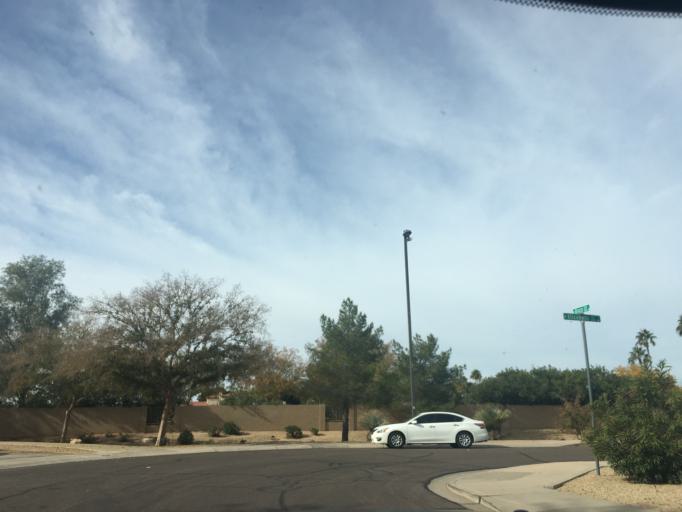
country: US
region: Arizona
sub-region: Maricopa County
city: Gilbert
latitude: 33.3521
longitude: -111.8091
